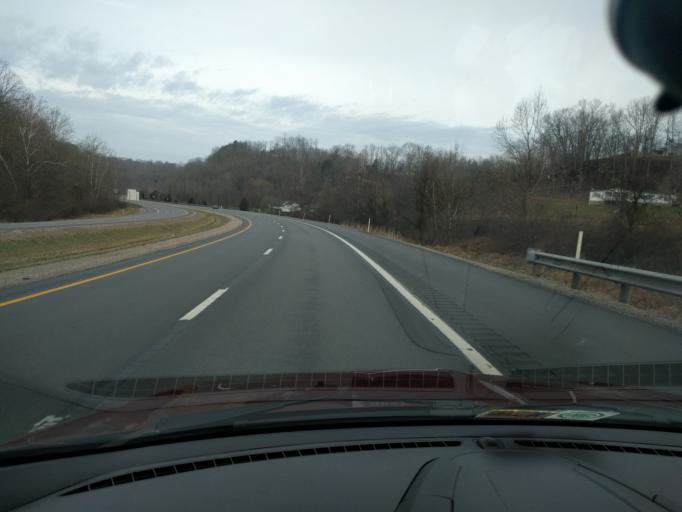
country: US
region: West Virginia
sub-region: Jackson County
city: Ripley
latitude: 38.7657
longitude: -81.7103
